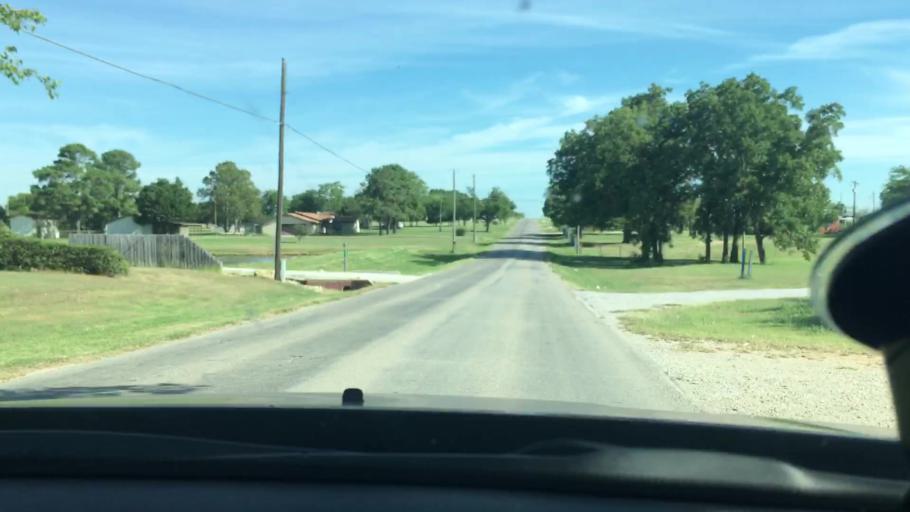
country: US
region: Oklahoma
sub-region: Carter County
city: Lone Grove
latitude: 34.1820
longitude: -97.2475
